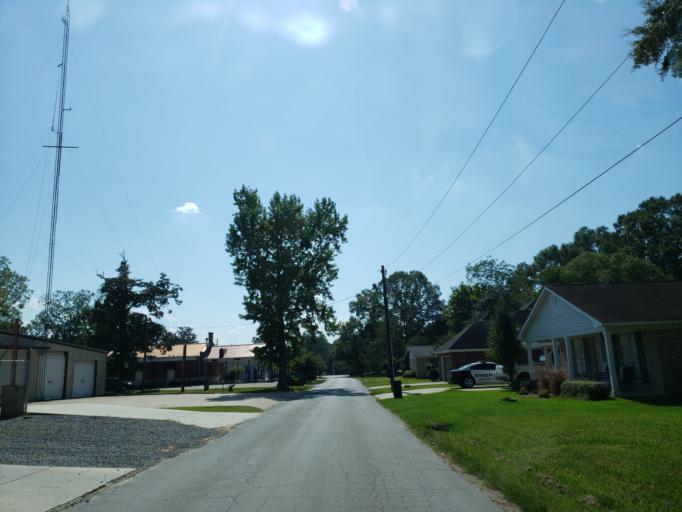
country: US
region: Mississippi
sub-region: Covington County
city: Collins
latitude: 31.5624
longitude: -89.4995
